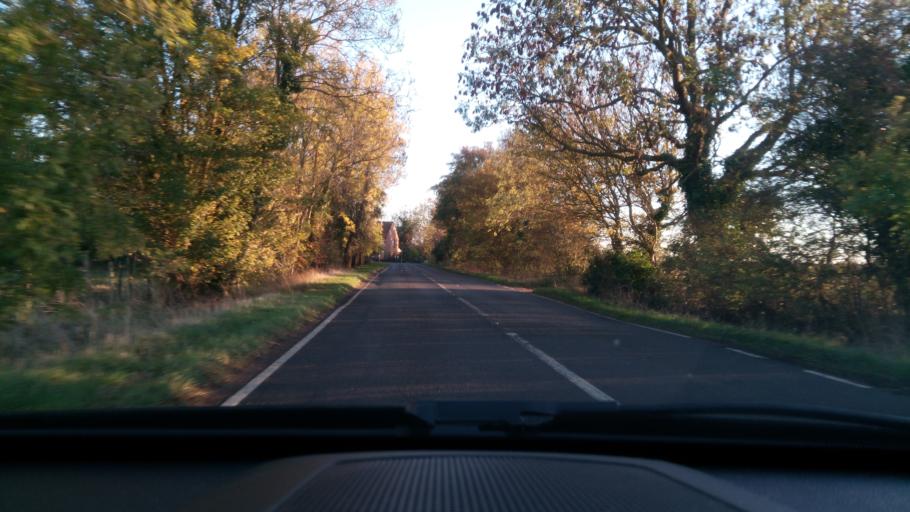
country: GB
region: England
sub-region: Peterborough
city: Helpston
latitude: 52.6363
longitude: -0.3583
